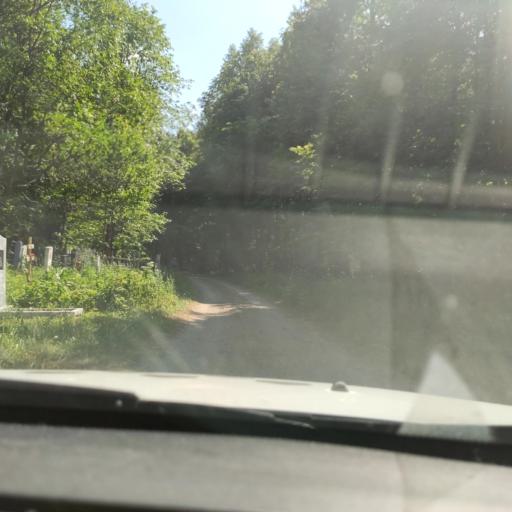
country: RU
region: Perm
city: Novyye Lyady
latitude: 58.1314
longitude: 56.4808
